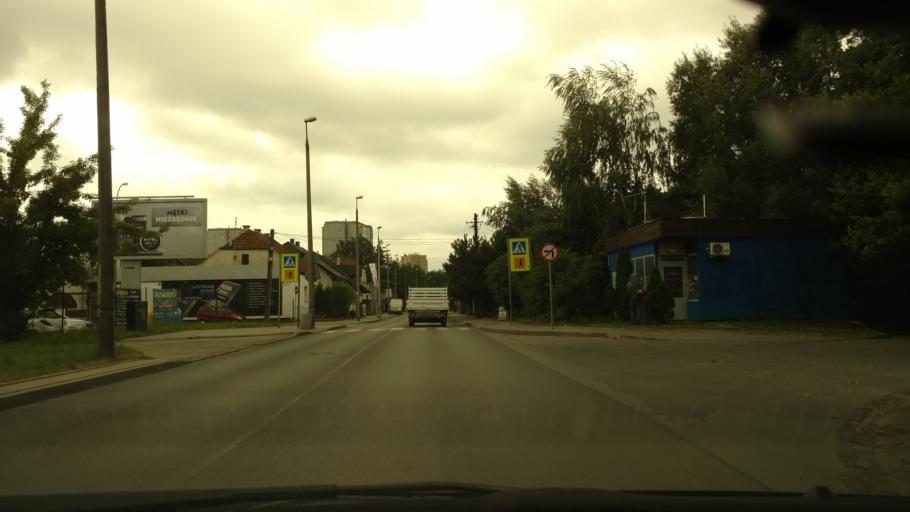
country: PL
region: Lesser Poland Voivodeship
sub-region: Krakow
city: Krakow
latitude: 50.0931
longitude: 19.9448
